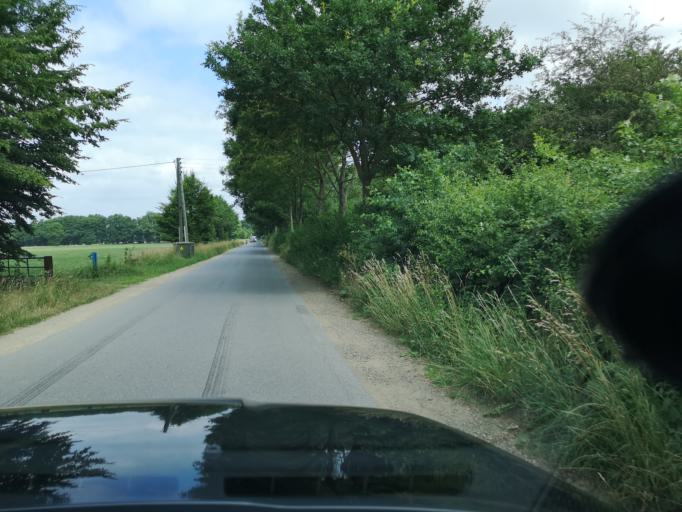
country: DE
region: North Rhine-Westphalia
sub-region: Regierungsbezirk Dusseldorf
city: Wesel
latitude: 51.6979
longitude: 6.6307
